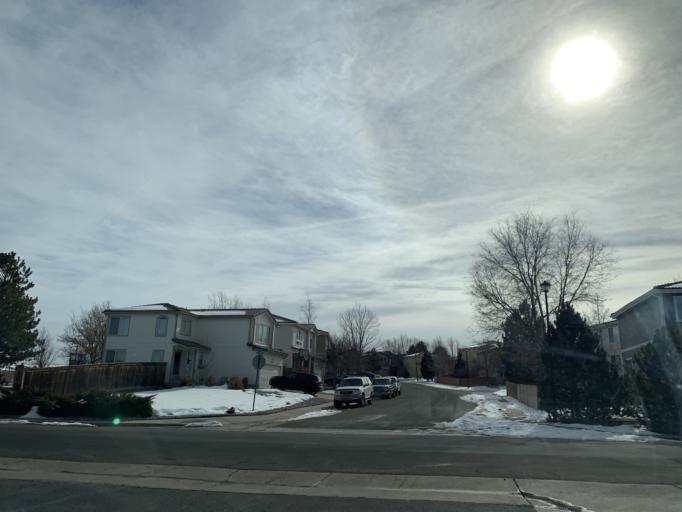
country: US
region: Colorado
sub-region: Douglas County
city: Carriage Club
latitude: 39.5370
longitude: -104.9358
